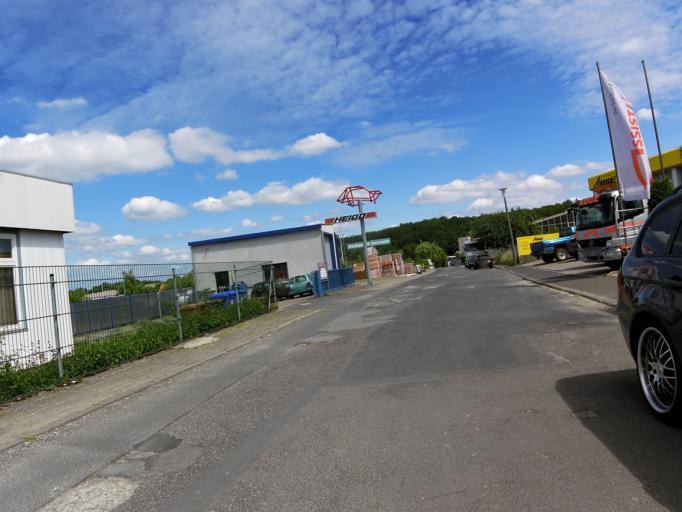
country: DE
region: Bavaria
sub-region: Regierungsbezirk Unterfranken
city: Kist
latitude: 49.7450
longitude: 9.8469
